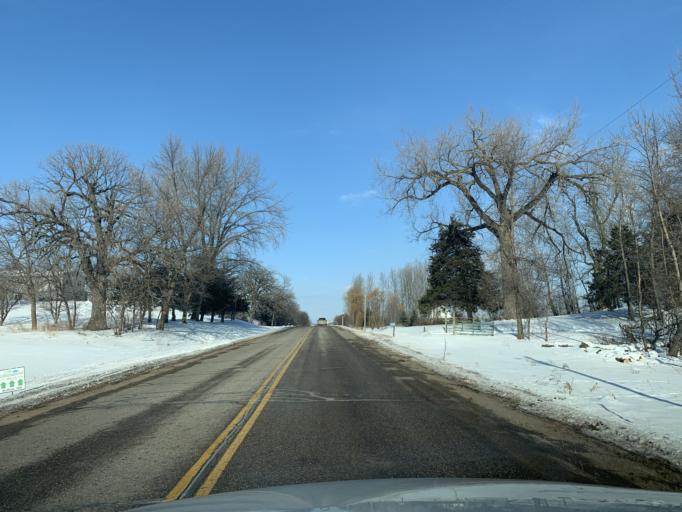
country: US
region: Minnesota
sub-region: Wright County
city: Buffalo
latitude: 45.1973
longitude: -93.8271
